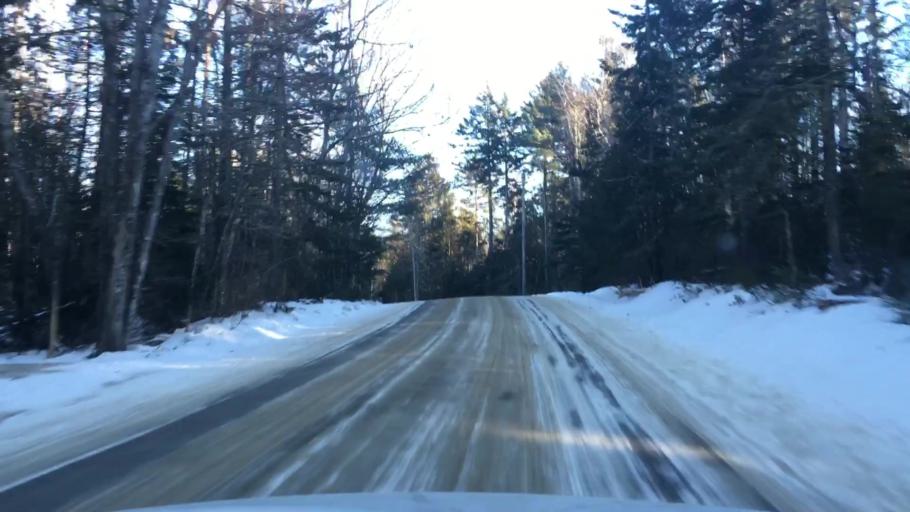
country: US
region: Maine
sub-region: Hancock County
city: Castine
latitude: 44.3828
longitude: -68.7325
